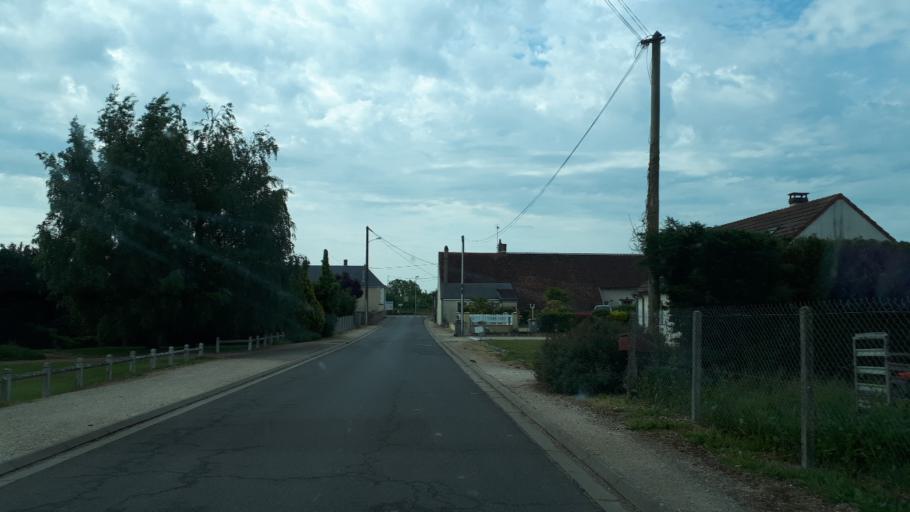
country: FR
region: Centre
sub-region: Departement du Loir-et-Cher
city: Villiers-sur-Loir
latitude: 47.7490
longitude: 0.9884
